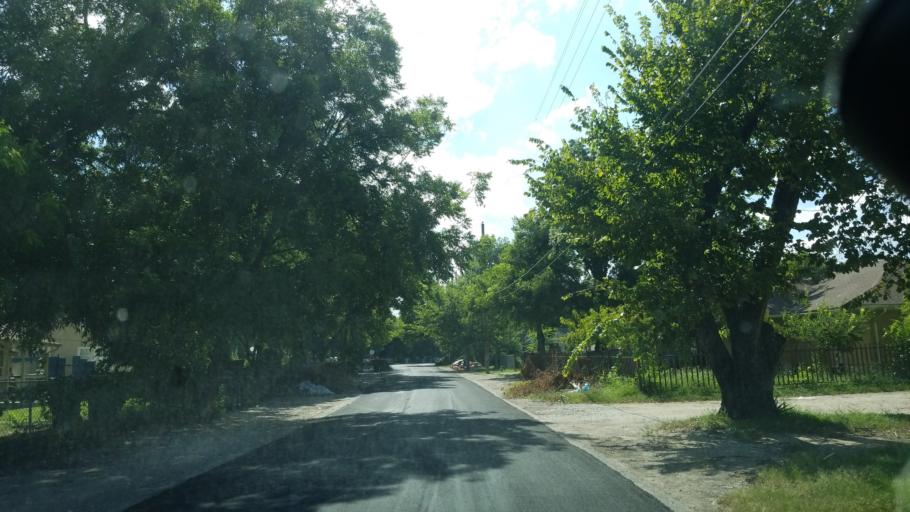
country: US
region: Texas
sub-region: Dallas County
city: Balch Springs
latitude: 32.7703
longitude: -96.6988
